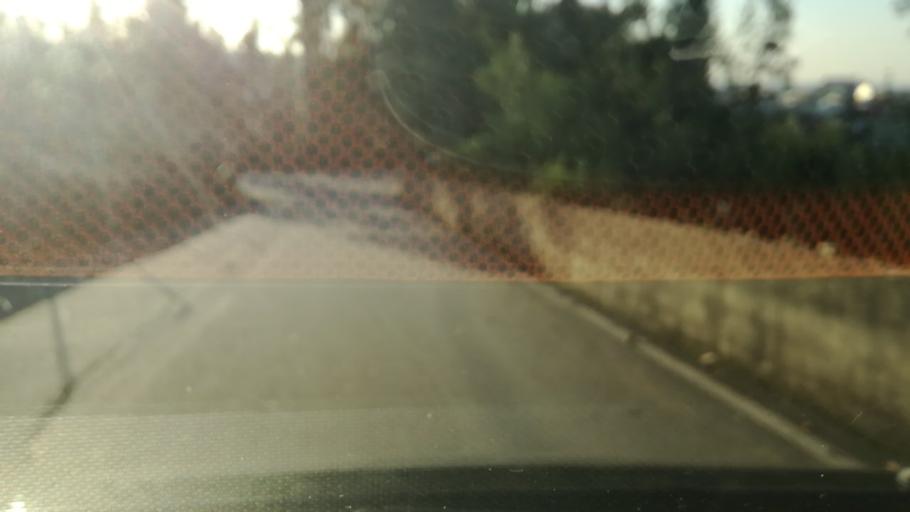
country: PT
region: Porto
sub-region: Trofa
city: Bougado
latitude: 41.3386
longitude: -8.5274
